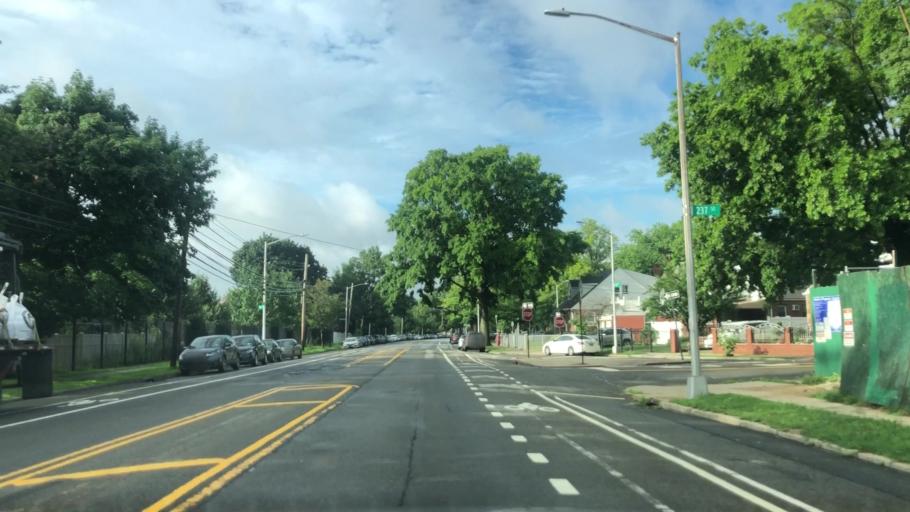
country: US
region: New York
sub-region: Nassau County
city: Bellerose Terrace
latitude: 40.7371
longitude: -73.7342
